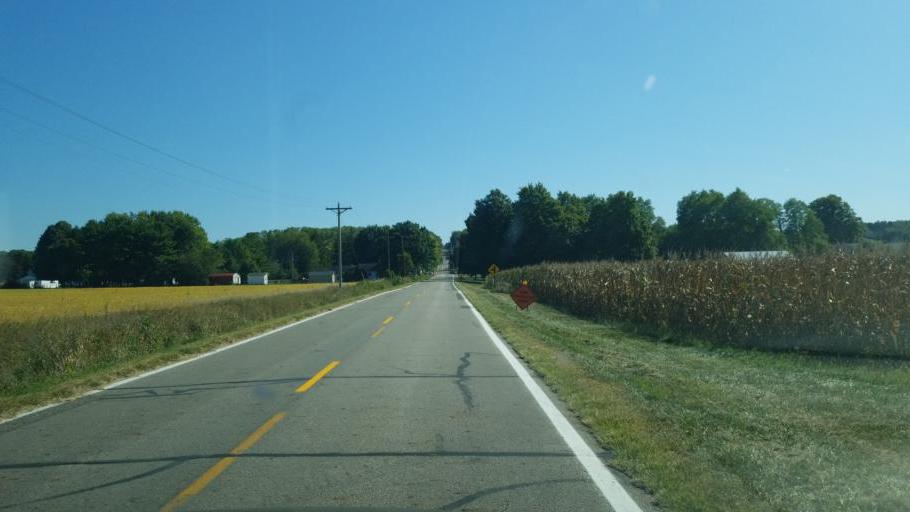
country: US
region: Ohio
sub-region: Champaign County
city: North Lewisburg
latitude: 40.2113
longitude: -83.6384
